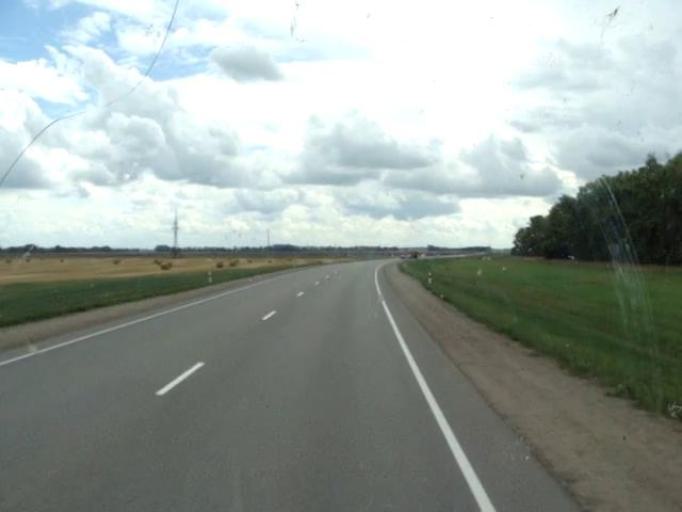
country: RU
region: Altai Krai
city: Shubenka
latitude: 52.6801
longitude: 85.0484
